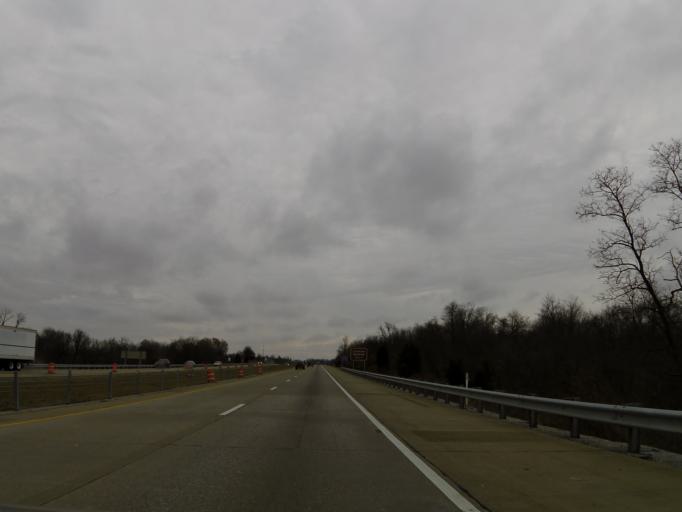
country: US
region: Indiana
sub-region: Dearborn County
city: Lawrenceburg
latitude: 39.0922
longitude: -84.8082
